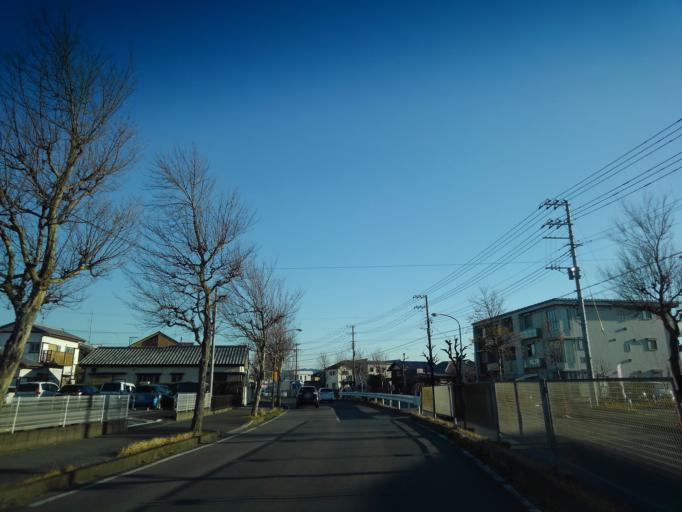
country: JP
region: Chiba
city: Kimitsu
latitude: 35.3224
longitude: 139.9116
